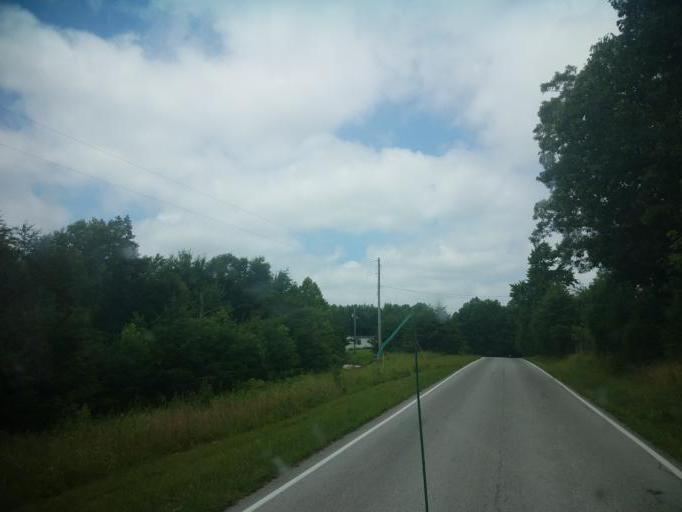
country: US
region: Kentucky
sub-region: Hart County
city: Munfordville
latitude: 37.3097
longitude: -85.9641
